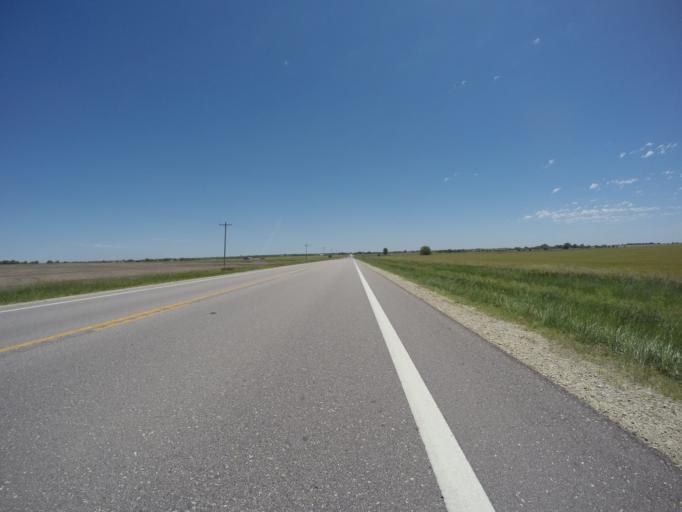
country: US
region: Kansas
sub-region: Republic County
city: Belleville
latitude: 39.8127
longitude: -97.6783
